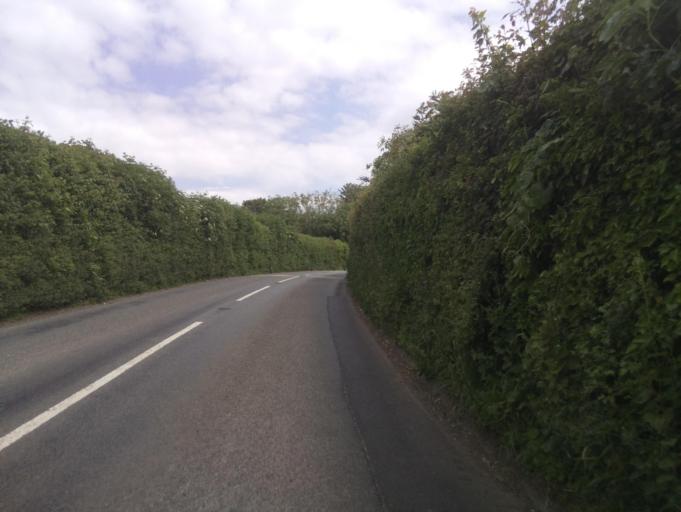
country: GB
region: England
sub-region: Somerset
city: Milborne Port
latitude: 51.0036
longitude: -2.4822
